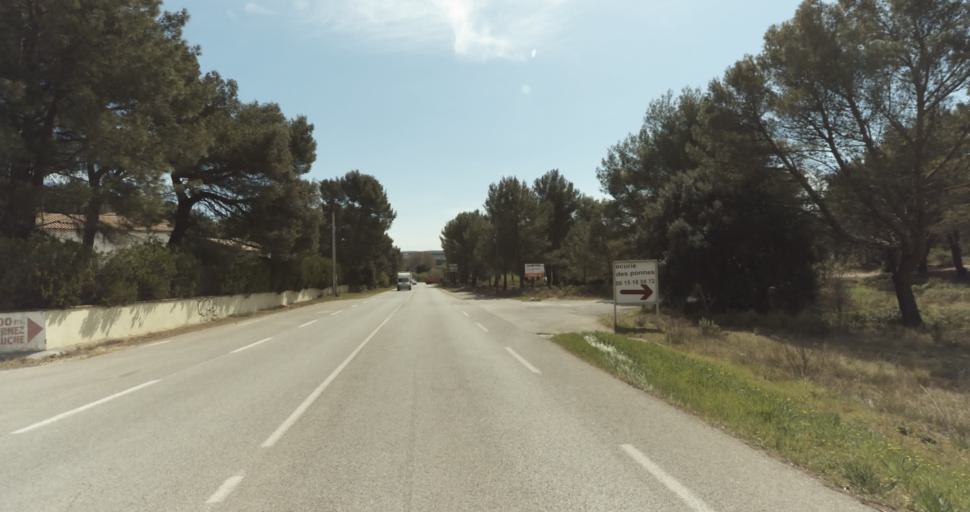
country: FR
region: Provence-Alpes-Cote d'Azur
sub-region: Departement des Bouches-du-Rhone
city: Lambesc
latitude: 43.6401
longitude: 5.2751
